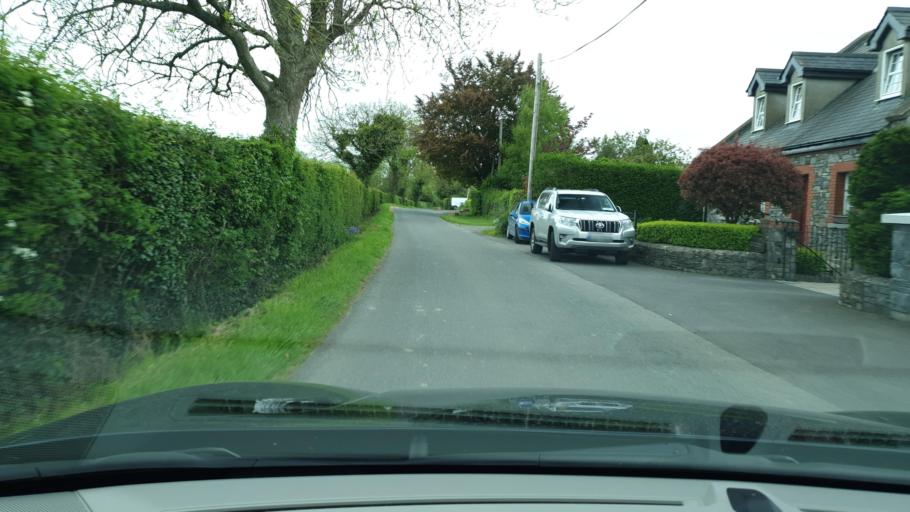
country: IE
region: Leinster
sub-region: An Mhi
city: Ratoath
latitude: 53.4915
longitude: -6.4955
